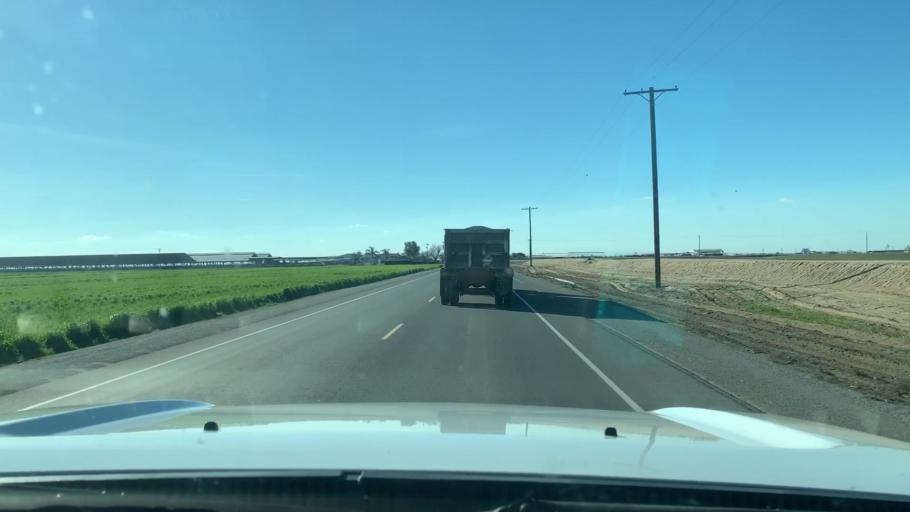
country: US
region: California
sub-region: Kings County
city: Corcoran
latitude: 36.2111
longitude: -119.5255
